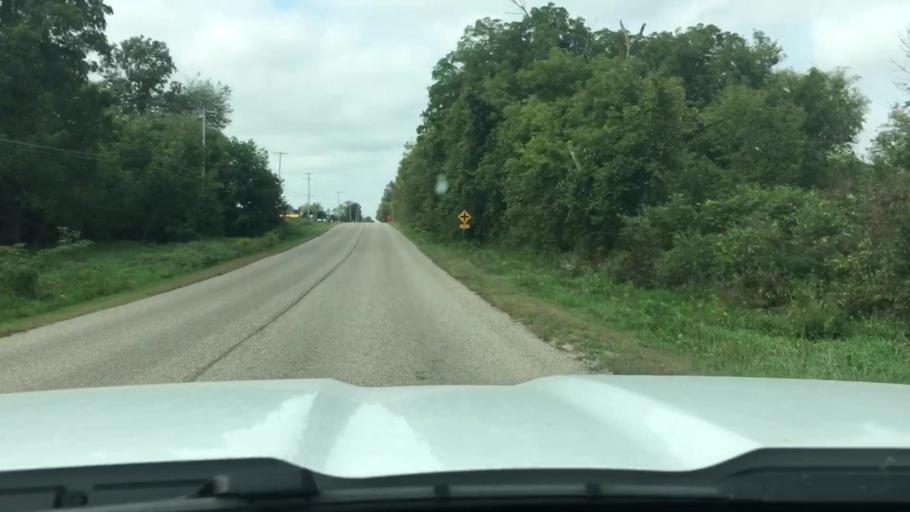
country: US
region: Michigan
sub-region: Eaton County
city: Potterville
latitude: 42.6256
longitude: -84.7031
